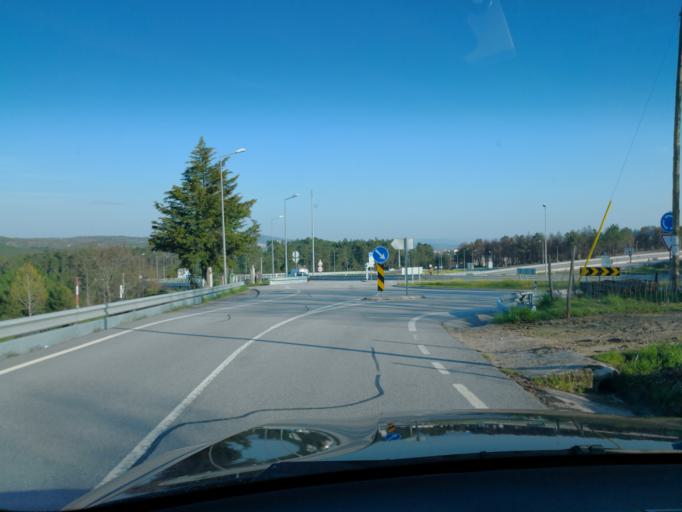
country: PT
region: Vila Real
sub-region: Sabrosa
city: Sabrosa
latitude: 41.3520
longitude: -7.6005
